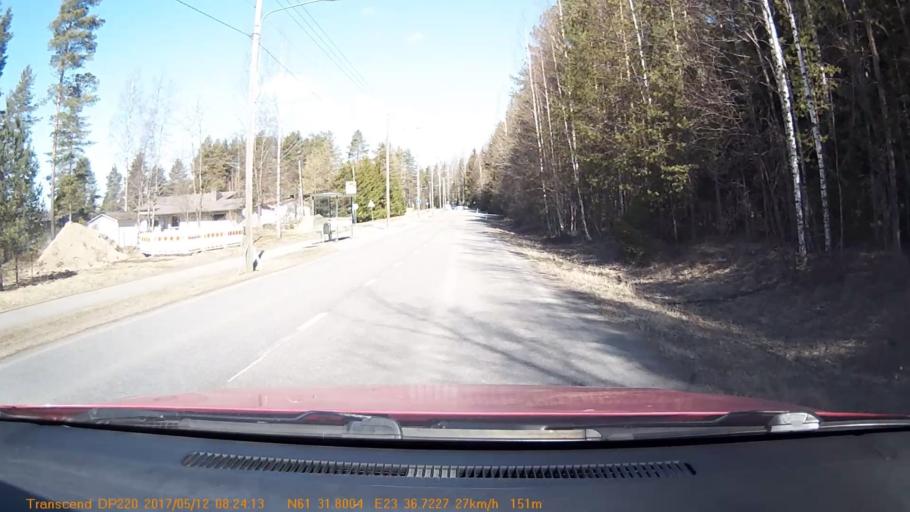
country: FI
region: Pirkanmaa
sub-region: Tampere
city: Yloejaervi
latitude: 61.5301
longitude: 23.6120
